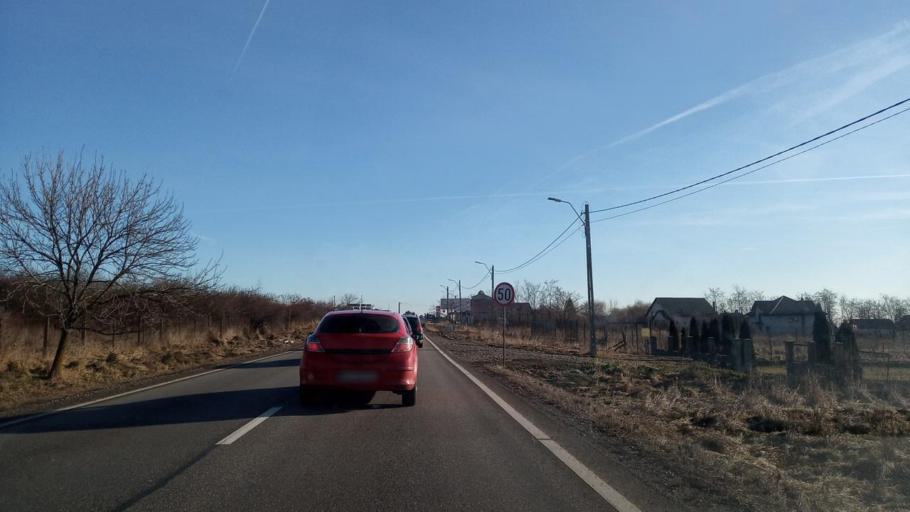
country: RO
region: Suceava
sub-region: Comuna Fantana Mare
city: Fantana Mare
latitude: 47.4308
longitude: 26.2956
